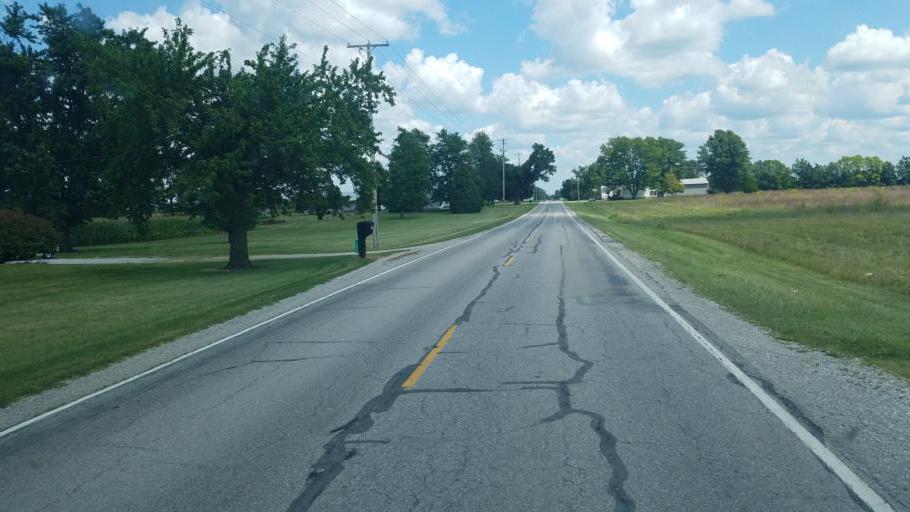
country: US
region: Ohio
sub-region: Marion County
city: Marion
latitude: 40.6303
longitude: -83.0416
